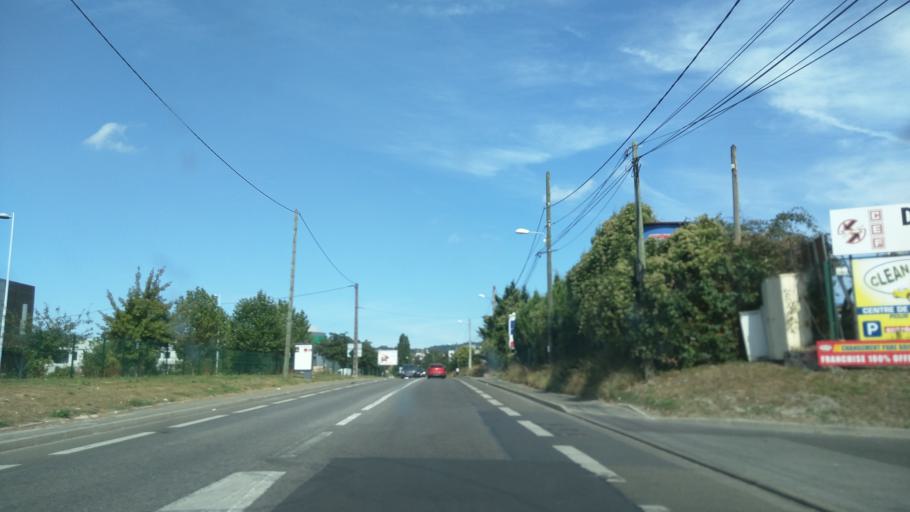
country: FR
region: Ile-de-France
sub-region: Departement des Yvelines
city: Sartrouville
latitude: 48.9552
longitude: 2.2054
